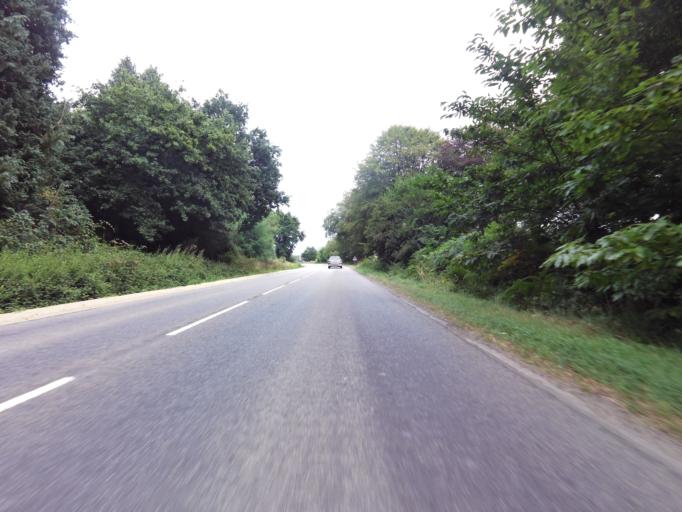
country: FR
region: Brittany
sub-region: Departement du Finistere
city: Douarnenez
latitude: 48.0808
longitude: -4.3608
